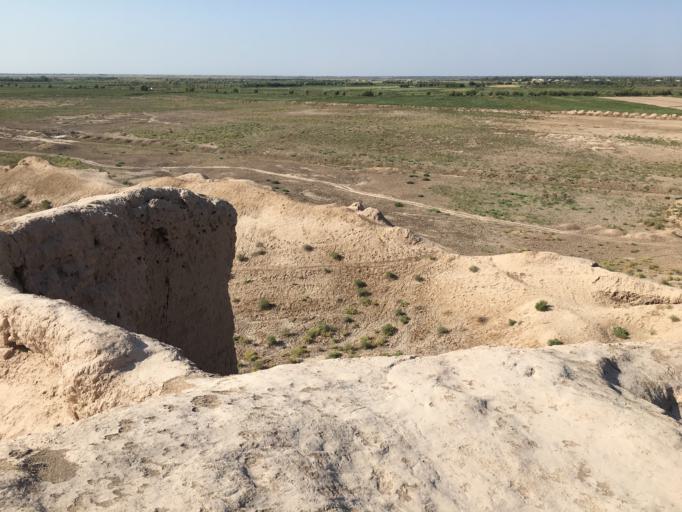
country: UZ
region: Karakalpakstan
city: Bo'ston Shahri
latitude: 41.9282
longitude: 60.8212
